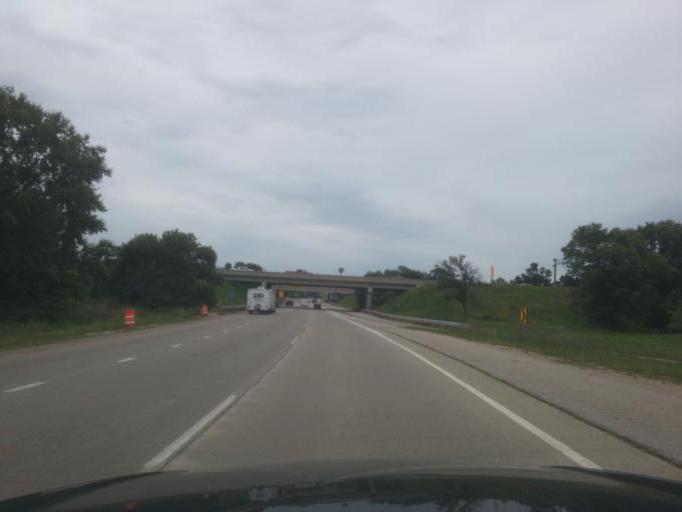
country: US
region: Wisconsin
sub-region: Dane County
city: McFarland
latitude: 43.0458
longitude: -89.2798
